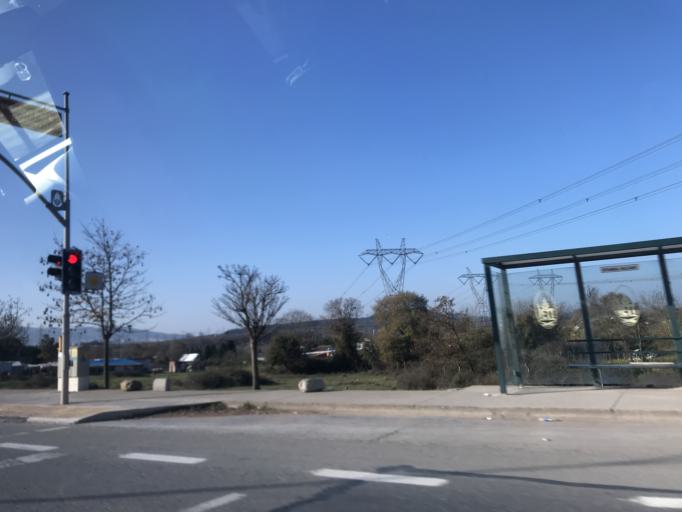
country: TR
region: Kocaeli
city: Balcik
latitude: 40.9362
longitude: 29.3627
